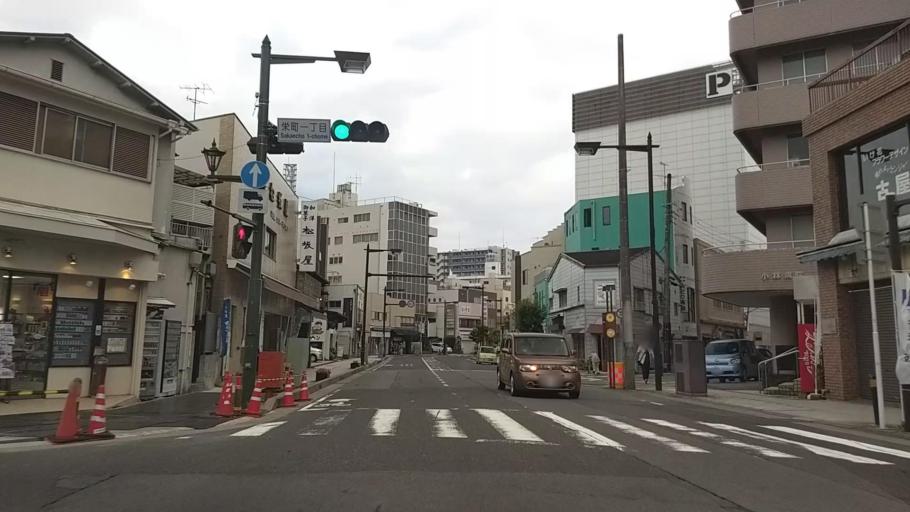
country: JP
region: Kanagawa
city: Odawara
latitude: 35.2539
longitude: 139.1587
